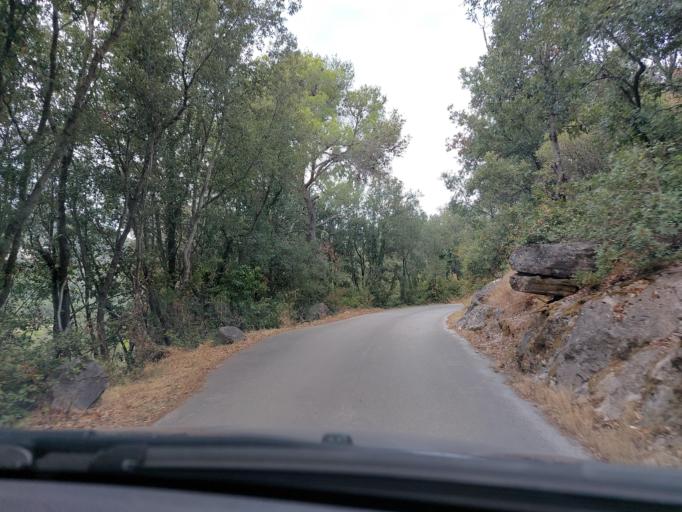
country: HR
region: Dubrovacko-Neretvanska
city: Smokvica
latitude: 42.7629
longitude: 16.9059
